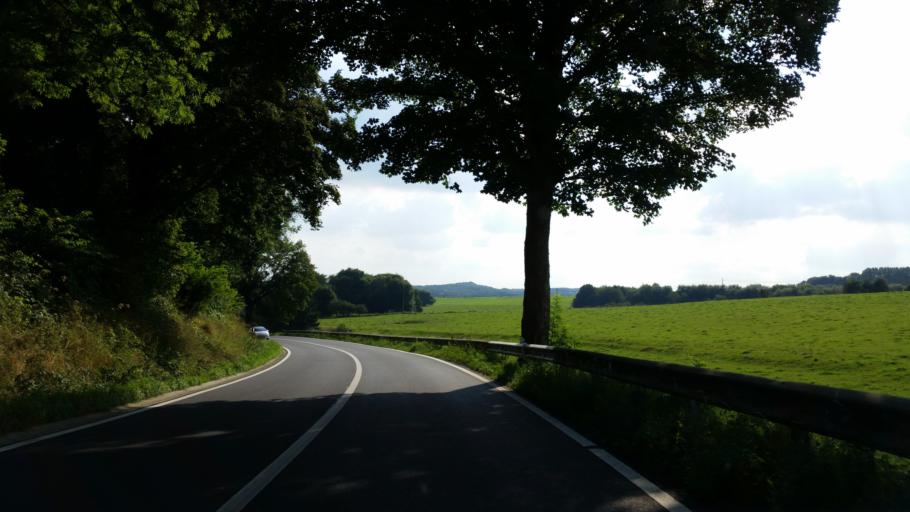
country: BE
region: Wallonia
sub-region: Province de Liege
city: Ouffet
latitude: 50.4341
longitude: 5.4588
